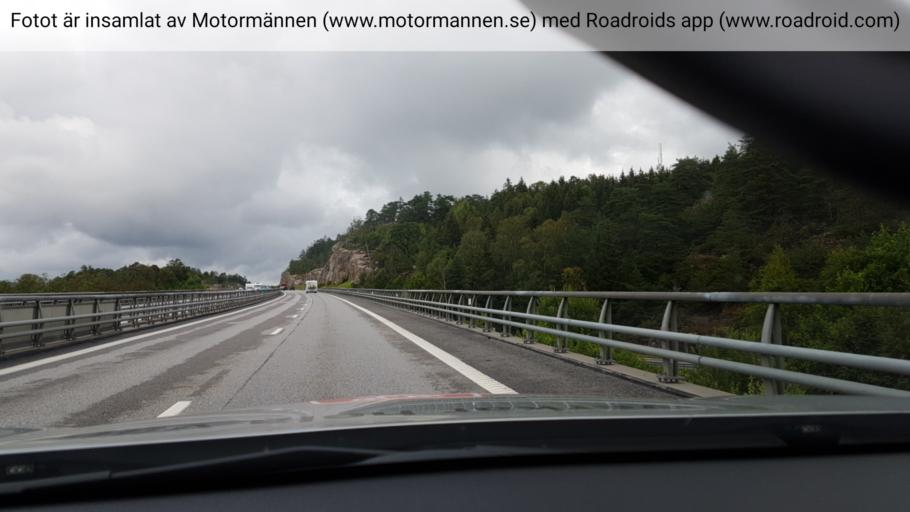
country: SE
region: Vaestra Goetaland
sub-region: Stromstads Kommun
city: Stroemstad
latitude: 58.9969
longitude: 11.2321
